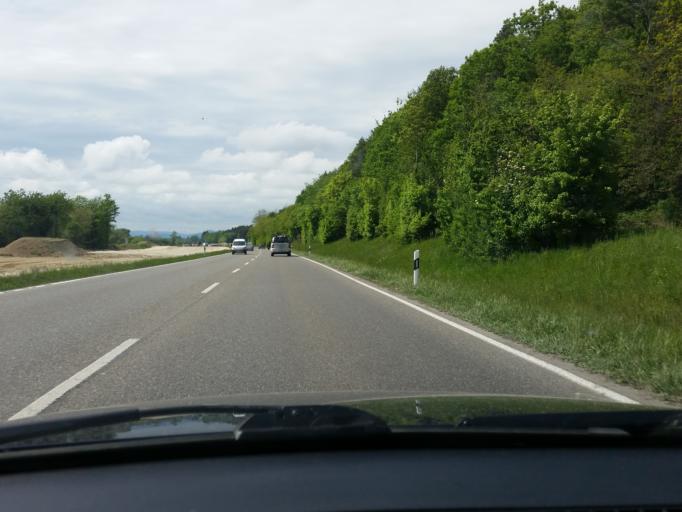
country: DE
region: Baden-Wuerttemberg
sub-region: Freiburg Region
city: Allensbach
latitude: 47.7253
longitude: 9.0560
